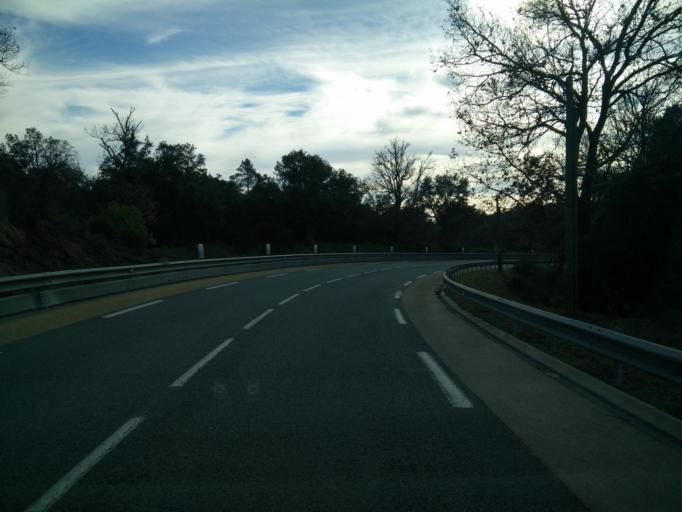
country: FR
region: Provence-Alpes-Cote d'Azur
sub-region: Departement du Var
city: Saint-Paul-en-Foret
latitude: 43.5551
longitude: 6.7026
